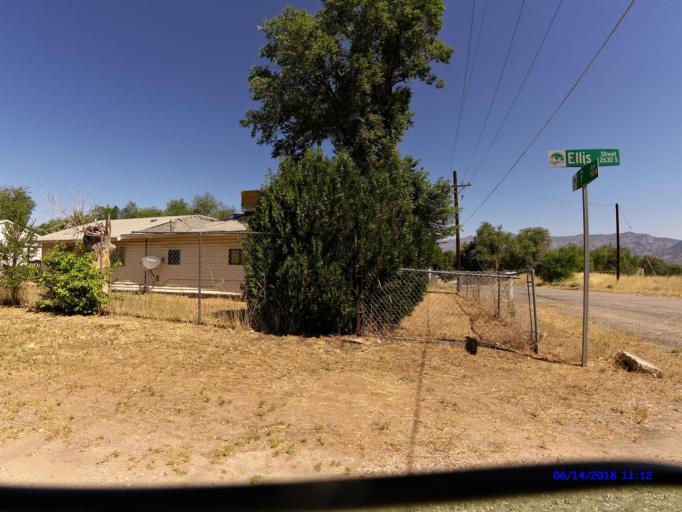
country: US
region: Utah
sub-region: Weber County
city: Ogden
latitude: 41.2185
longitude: -111.9972
